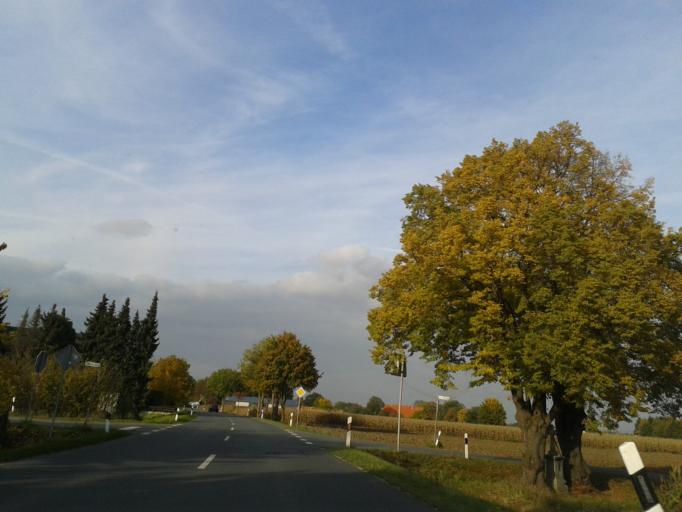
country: DE
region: North Rhine-Westphalia
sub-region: Regierungsbezirk Detmold
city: Salzkotten
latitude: 51.7311
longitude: 8.6635
